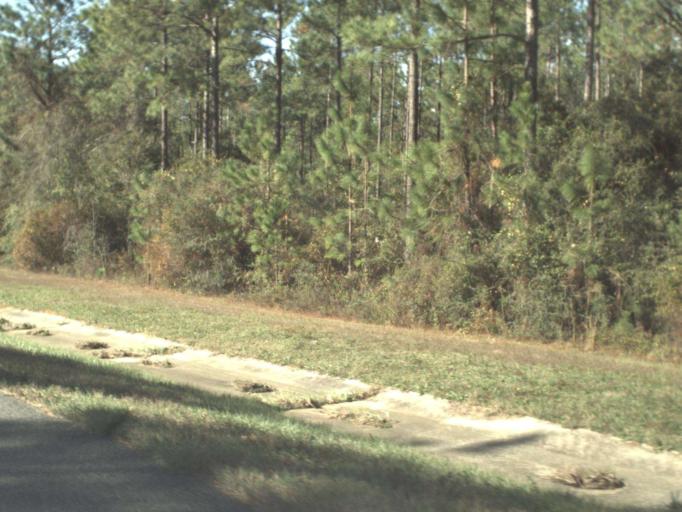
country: US
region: Florida
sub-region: Okaloosa County
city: Crestview
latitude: 30.8500
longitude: -86.7624
